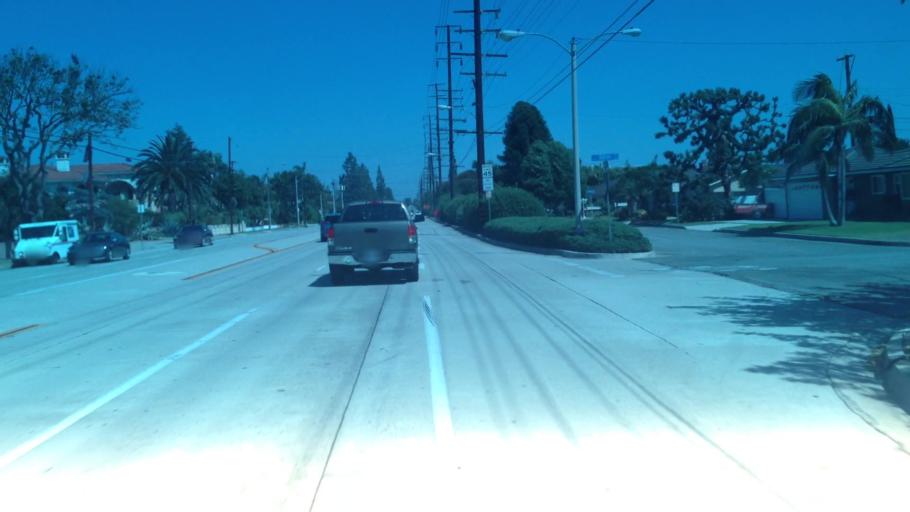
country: US
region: California
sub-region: Los Angeles County
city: Downey
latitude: 33.9437
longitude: -118.1098
